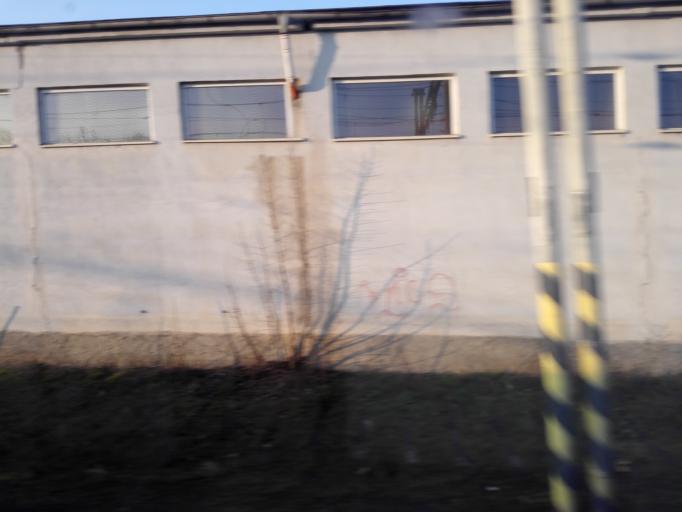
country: CZ
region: Ustecky
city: Lovosice
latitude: 50.5110
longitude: 14.0535
